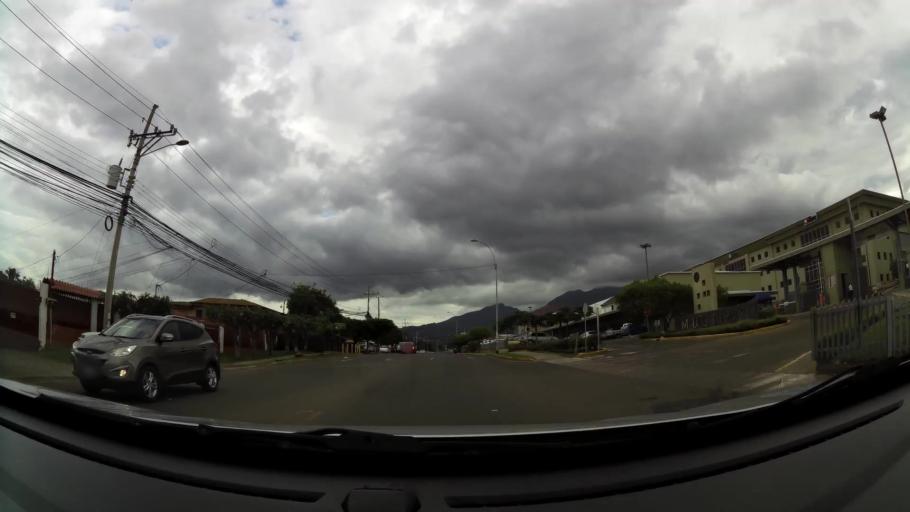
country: CR
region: San Jose
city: Santa Ana
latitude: 9.9497
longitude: -84.1633
